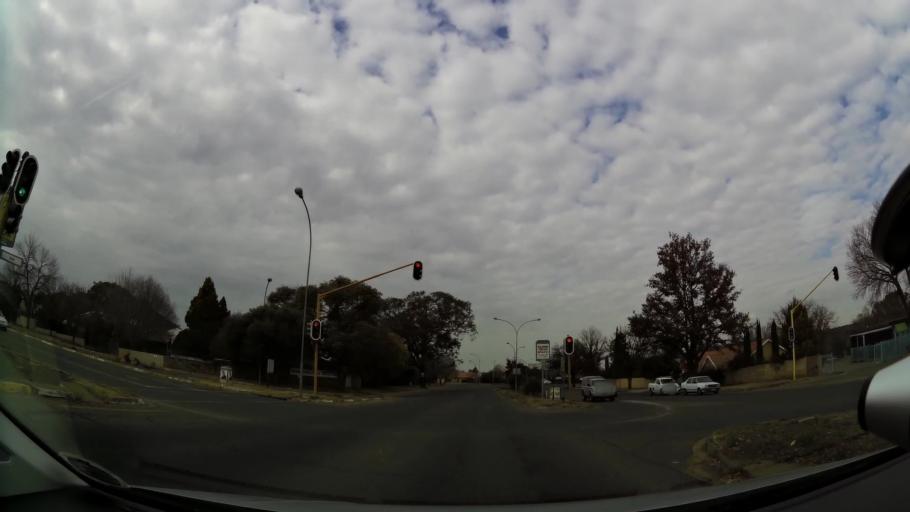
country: ZA
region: Orange Free State
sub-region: Mangaung Metropolitan Municipality
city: Bloemfontein
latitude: -29.0842
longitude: 26.2256
